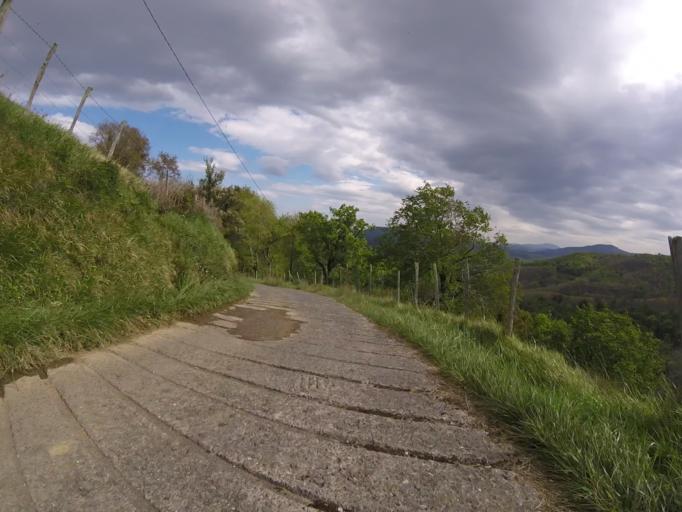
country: ES
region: Basque Country
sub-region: Provincia de Guipuzcoa
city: Zarautz
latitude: 43.2519
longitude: -2.1800
